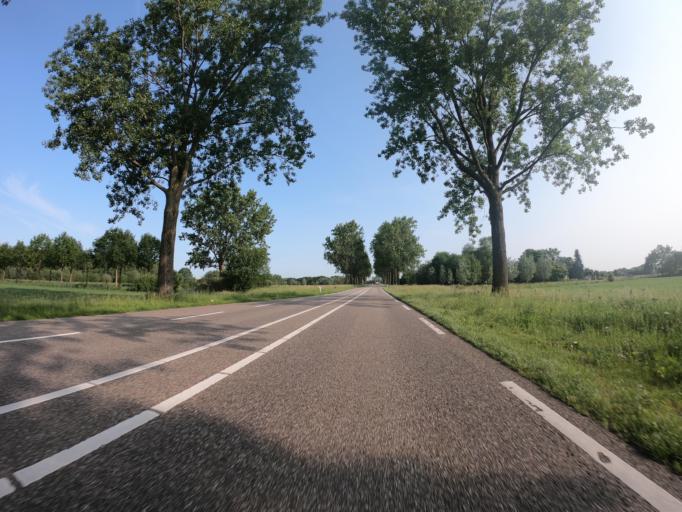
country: NL
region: North Brabant
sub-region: Gemeente Landerd
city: Reek
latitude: 51.7682
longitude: 5.6682
